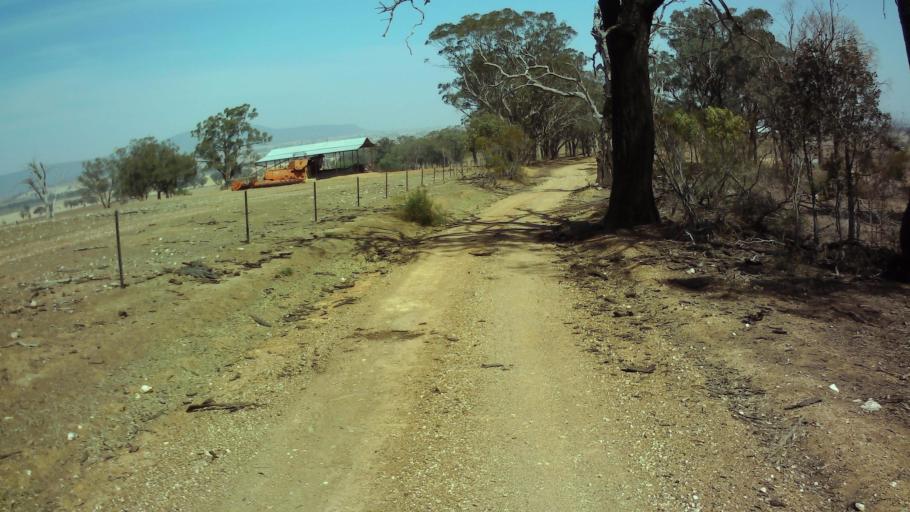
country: AU
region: New South Wales
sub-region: Weddin
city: Grenfell
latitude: -33.8939
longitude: 148.1144
